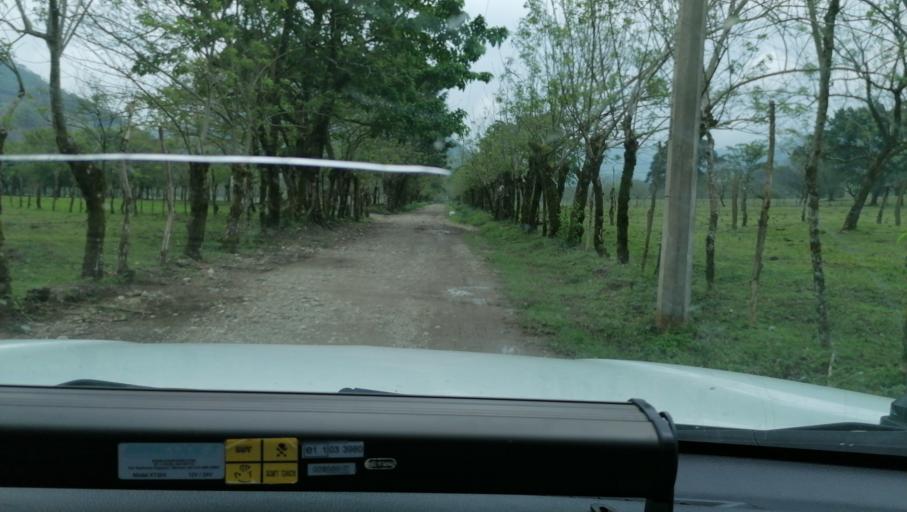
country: MX
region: Chiapas
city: Ixtacomitan
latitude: 17.3647
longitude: -93.1751
